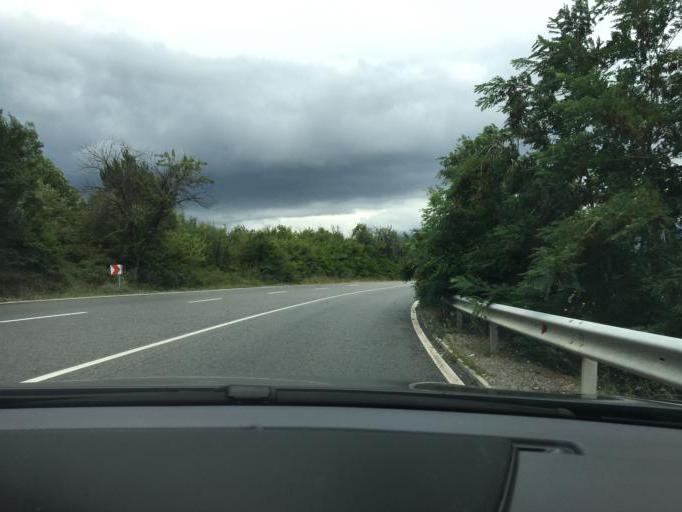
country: BG
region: Kyustendil
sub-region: Obshtina Bobovdol
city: Bobovdol
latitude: 42.2674
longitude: 22.9476
